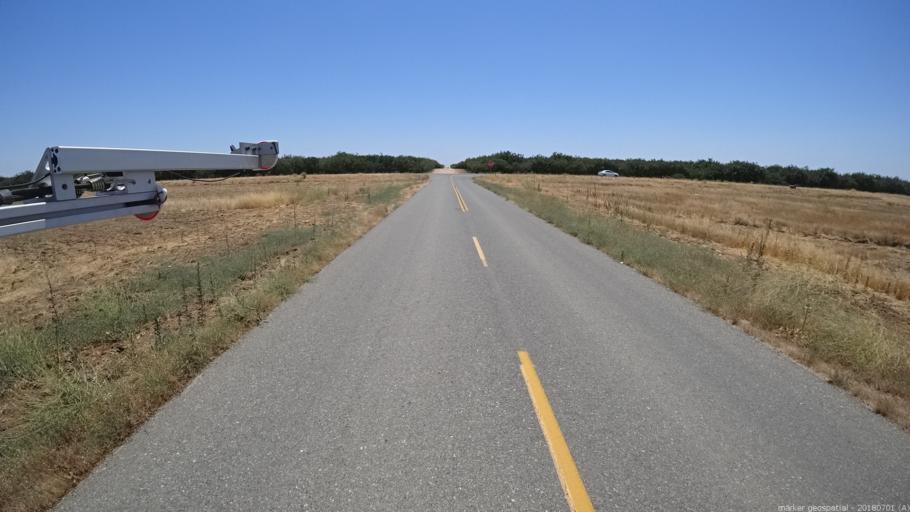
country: US
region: California
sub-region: Madera County
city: Madera Acres
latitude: 37.0549
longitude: -120.0201
